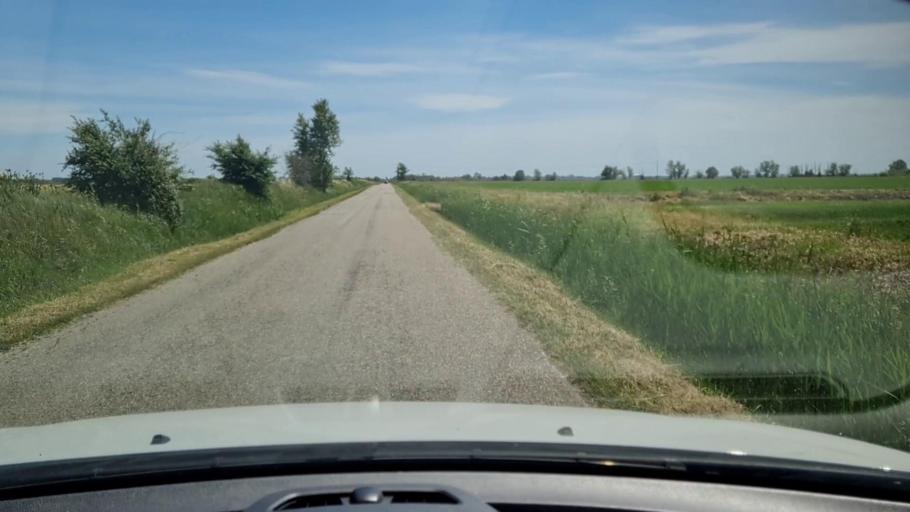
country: FR
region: Languedoc-Roussillon
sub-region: Departement du Gard
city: Saint-Gilles
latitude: 43.6148
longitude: 4.4259
